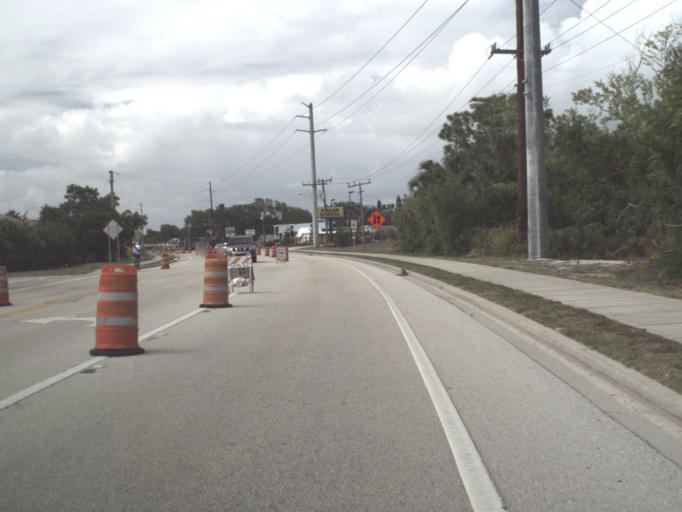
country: US
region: Florida
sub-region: Brevard County
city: Indian Harbour Beach
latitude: 28.1539
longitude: -80.5999
